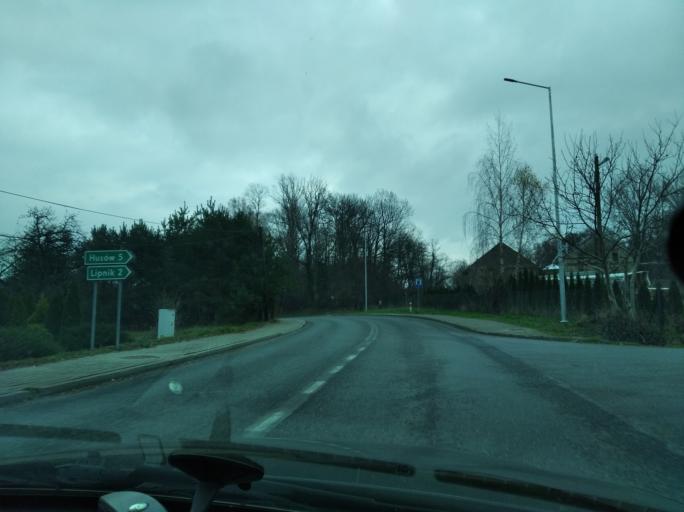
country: PL
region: Subcarpathian Voivodeship
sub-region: Powiat przeworski
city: Sietesz
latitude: 49.9999
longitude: 22.3516
